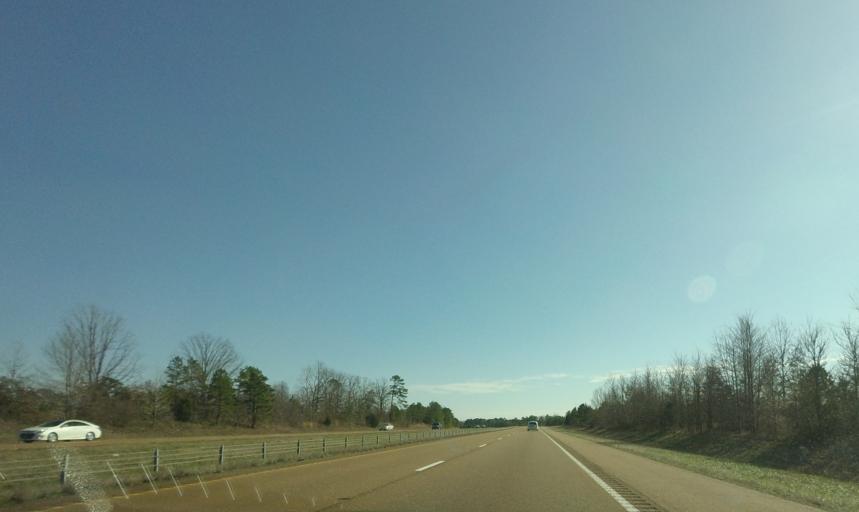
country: US
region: Mississippi
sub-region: Union County
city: New Albany
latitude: 34.5267
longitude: -89.0796
